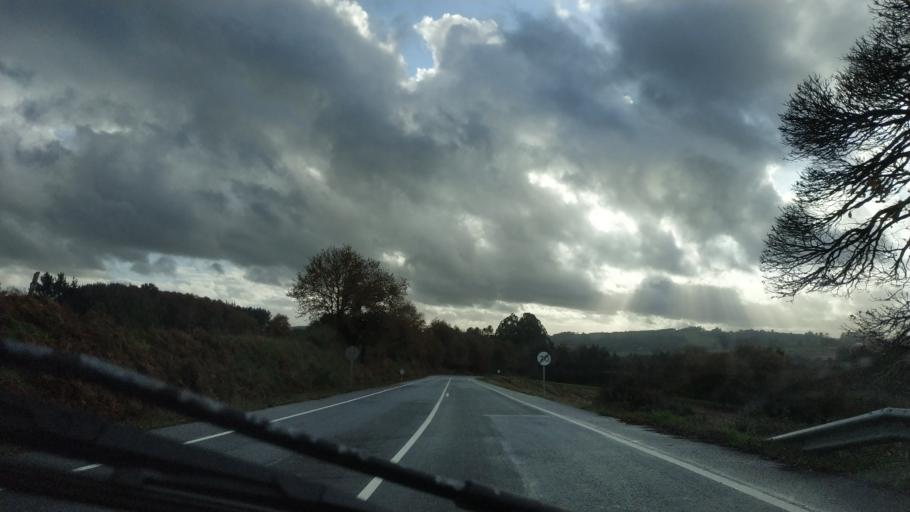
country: ES
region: Galicia
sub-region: Provincia da Coruna
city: Boimorto
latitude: 42.9676
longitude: -8.1428
